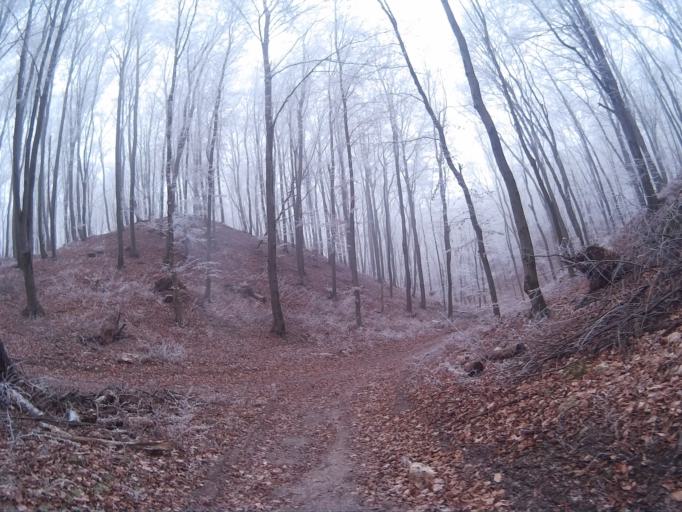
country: HU
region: Komarom-Esztergom
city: Oroszlany
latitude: 47.3966
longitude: 18.3188
